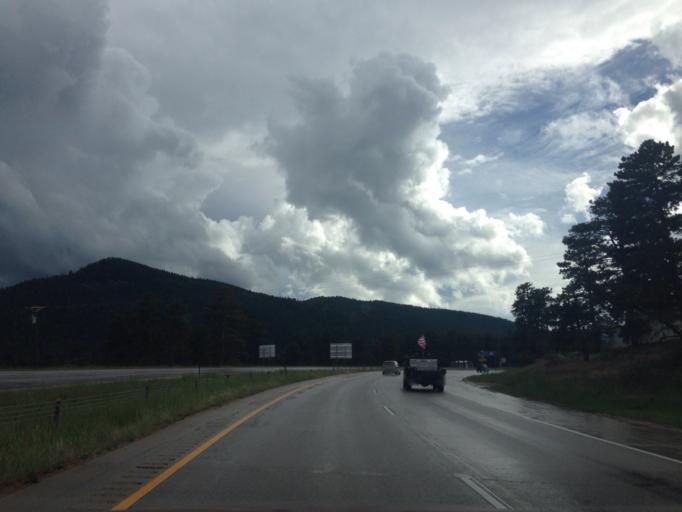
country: US
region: Colorado
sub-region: Jefferson County
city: Indian Hills
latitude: 39.5482
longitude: -105.2561
